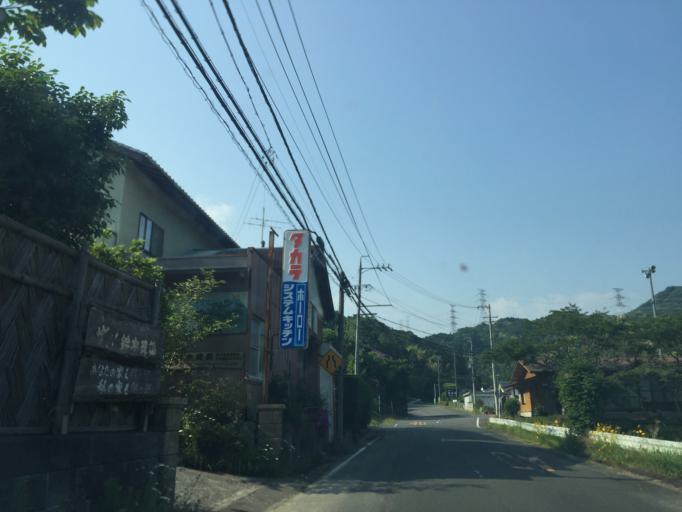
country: JP
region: Shizuoka
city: Kakegawa
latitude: 34.8328
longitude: 138.0422
